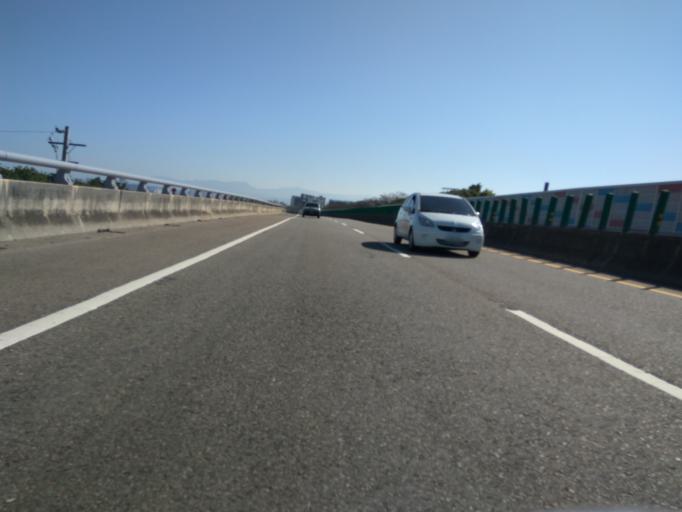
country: TW
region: Taiwan
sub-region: Hsinchu
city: Hsinchu
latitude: 24.8307
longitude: 120.9576
